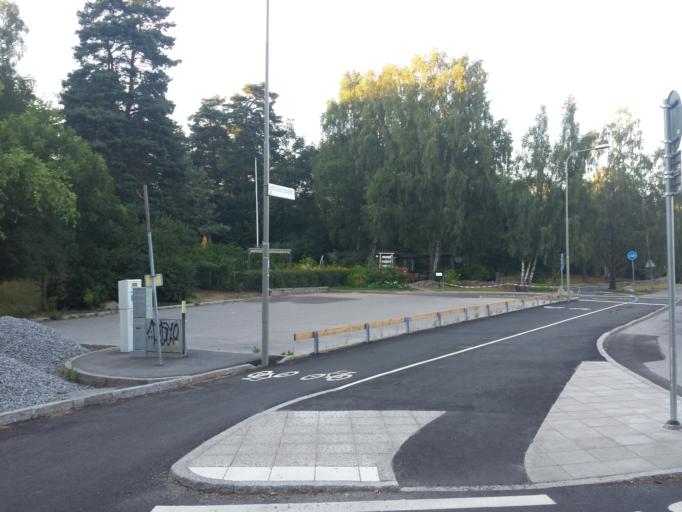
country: SE
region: Stockholm
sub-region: Stockholms Kommun
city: OEstermalm
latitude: 59.3493
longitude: 18.0803
